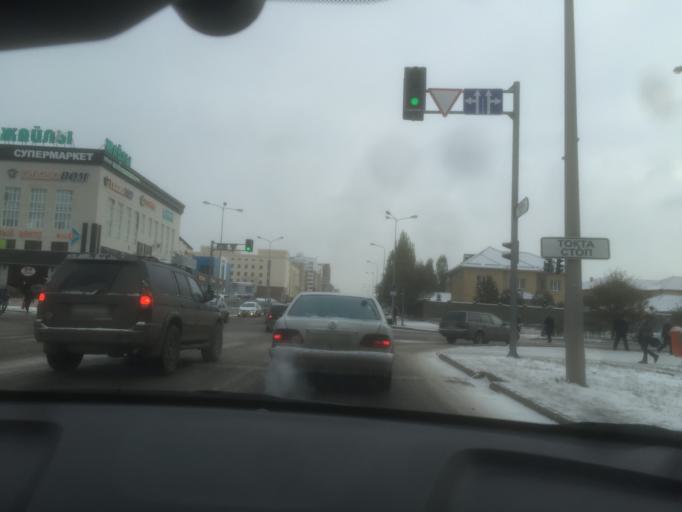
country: KZ
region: Astana Qalasy
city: Astana
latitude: 51.1445
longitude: 71.4730
